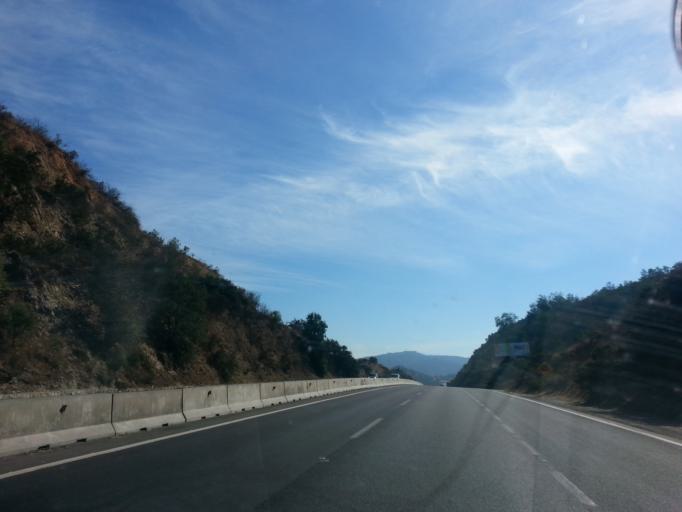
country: CL
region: Valparaiso
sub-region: Provincia de Marga Marga
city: Quilpue
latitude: -33.2845
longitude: -71.4260
